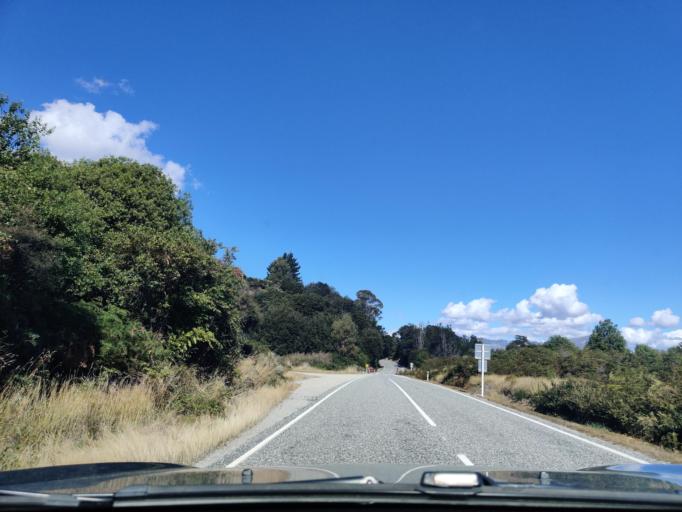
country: NZ
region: Otago
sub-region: Queenstown-Lakes District
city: Queenstown
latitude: -44.9906
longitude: 168.4317
